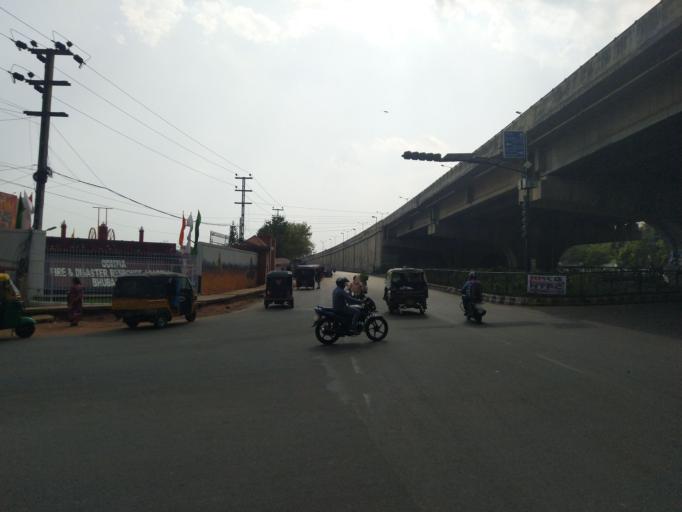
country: IN
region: Odisha
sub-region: Khordha
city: Bhubaneshwar
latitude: 20.2796
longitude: 85.7994
